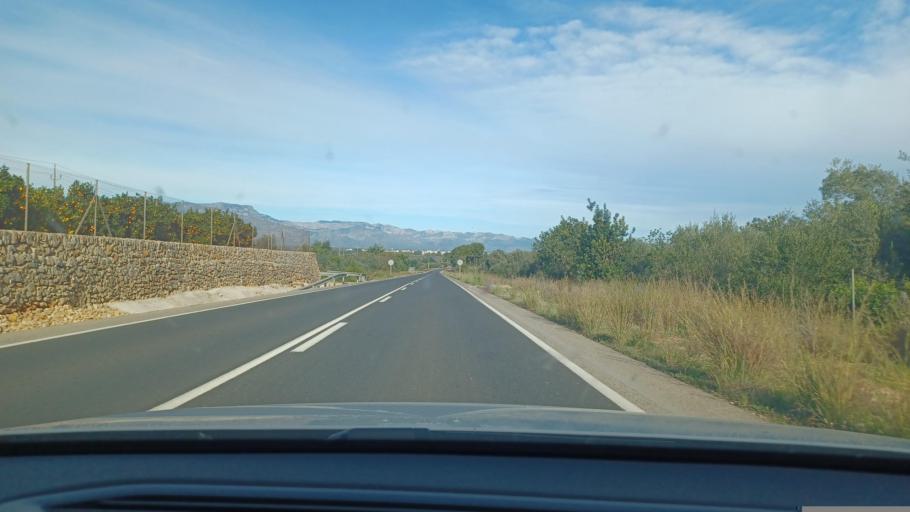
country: ES
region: Catalonia
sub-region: Provincia de Tarragona
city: Santa Barbara
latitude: 40.6834
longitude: 0.5102
